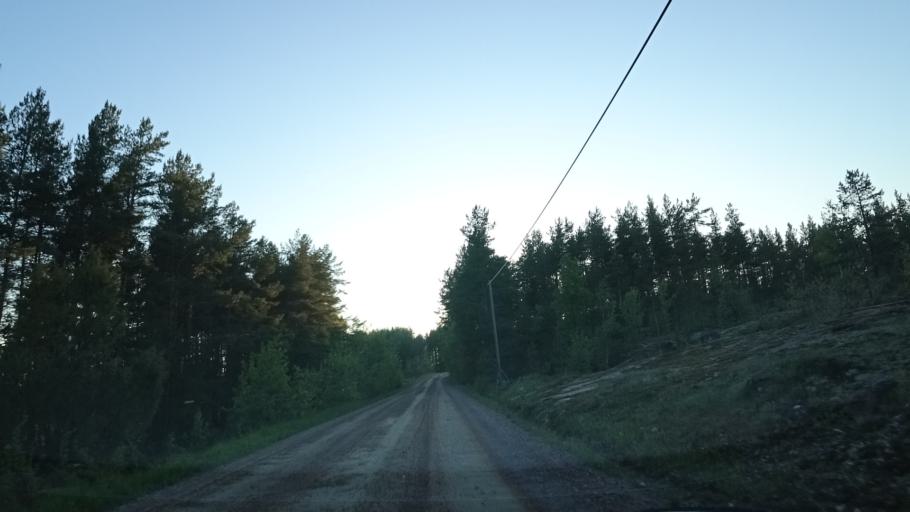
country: FI
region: Uusimaa
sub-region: Helsinki
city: Siuntio
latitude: 60.0637
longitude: 24.2247
